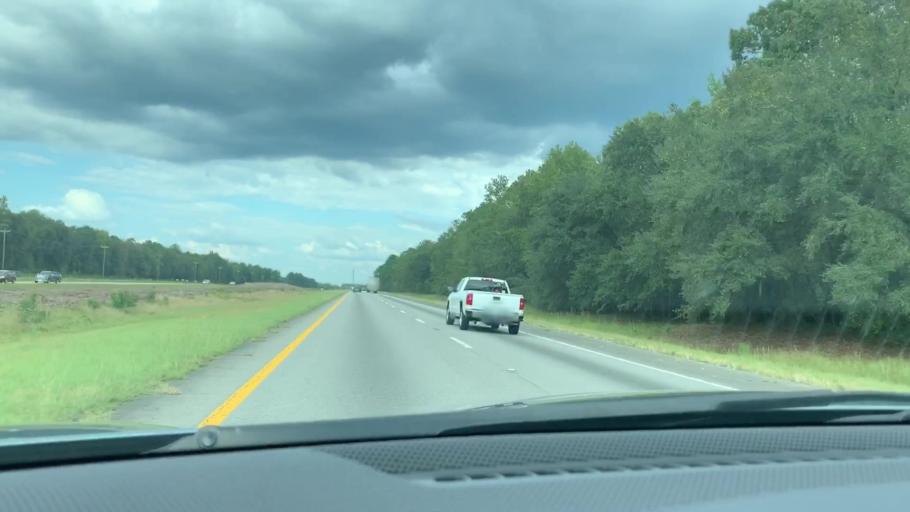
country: US
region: South Carolina
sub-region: Jasper County
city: Ridgeland
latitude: 32.5533
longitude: -80.9468
